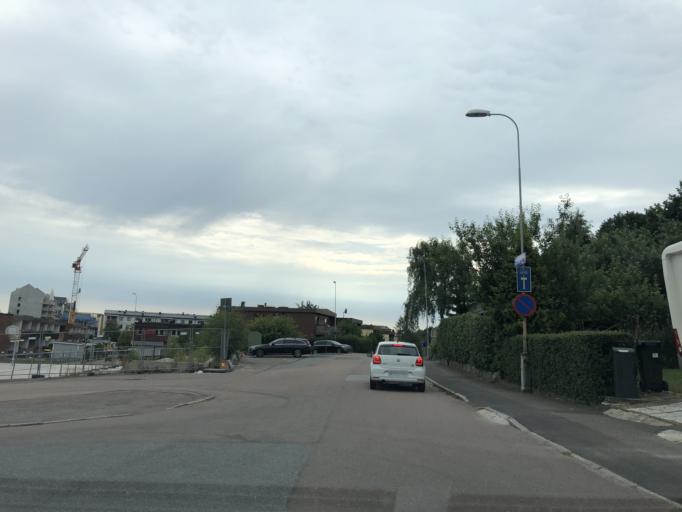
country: SE
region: Vaestra Goetaland
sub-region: Goteborg
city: Majorna
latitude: 57.7276
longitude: 11.9257
